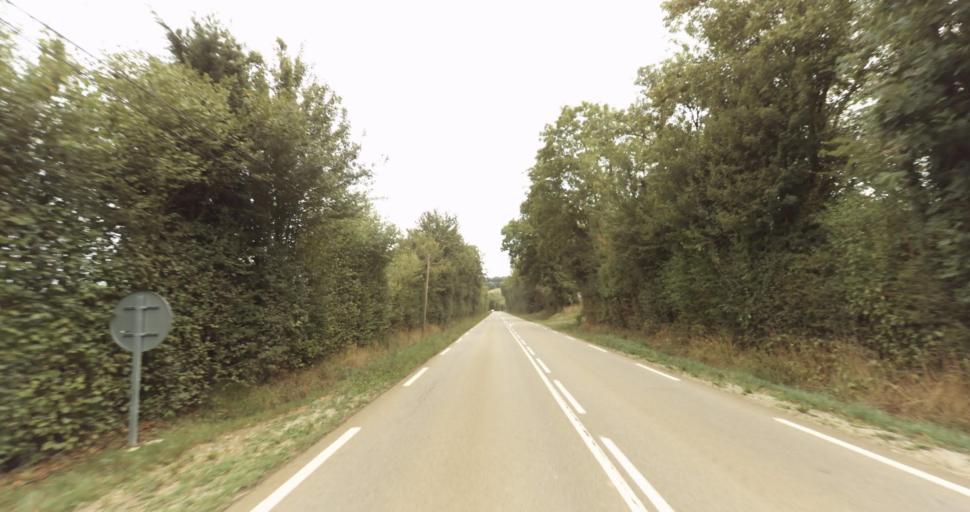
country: FR
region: Lower Normandy
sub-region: Departement de l'Orne
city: Gace
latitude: 48.7623
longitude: 0.3361
